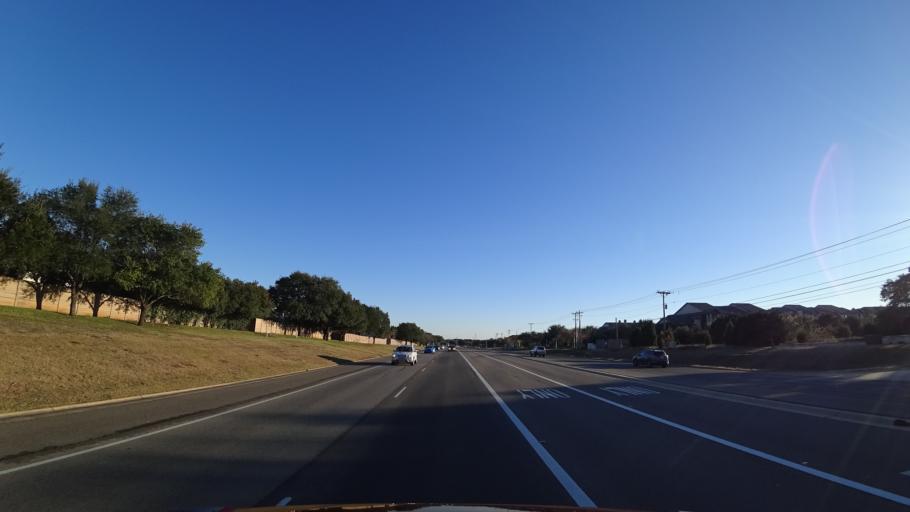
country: US
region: Texas
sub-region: Williamson County
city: Brushy Creek
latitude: 30.4909
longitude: -97.7721
